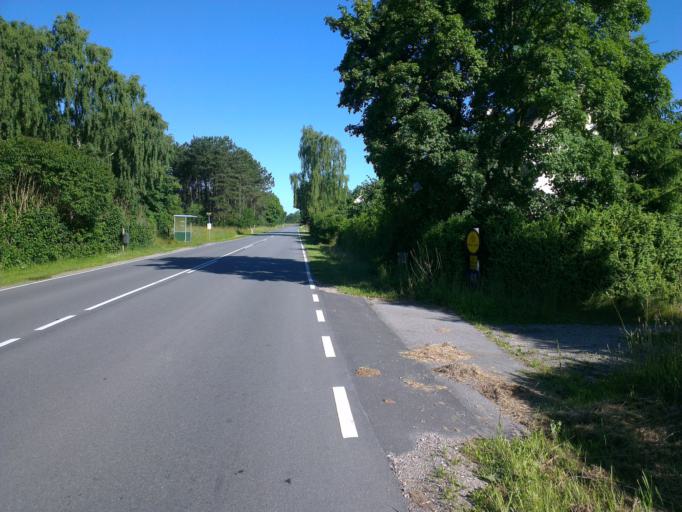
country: DK
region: Capital Region
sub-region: Frederikssund Kommune
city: Jaegerspris
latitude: 55.8941
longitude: 11.9535
